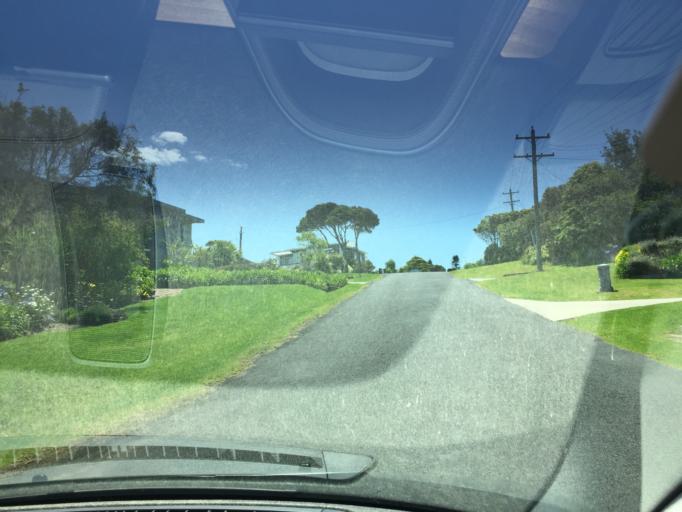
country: AU
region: New South Wales
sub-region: Bega Valley
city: Merimbula
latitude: -36.8966
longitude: 149.9266
